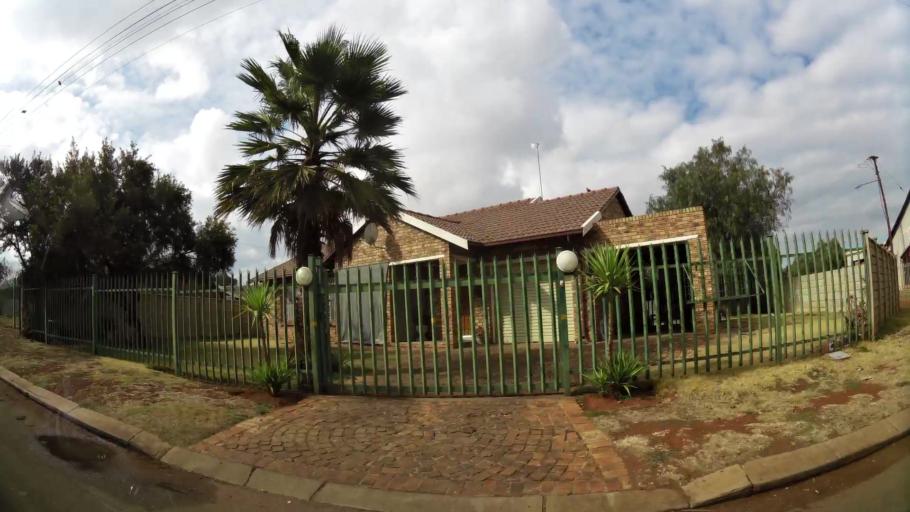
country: ZA
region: Gauteng
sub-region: Sedibeng District Municipality
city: Meyerton
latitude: -26.6000
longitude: 28.0398
